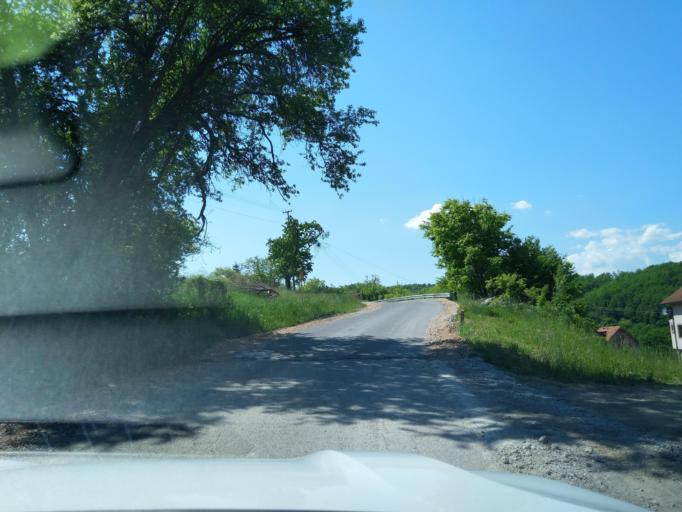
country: RS
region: Central Serbia
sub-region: Zlatiborski Okrug
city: Uzice
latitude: 43.8602
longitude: 19.9306
